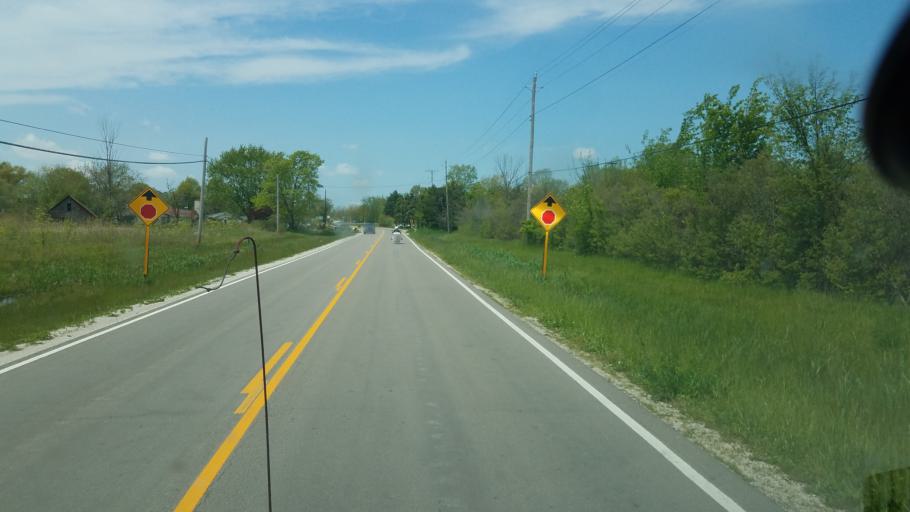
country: US
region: Ohio
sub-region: Ottawa County
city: Port Clinton
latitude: 41.5260
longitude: -83.0098
